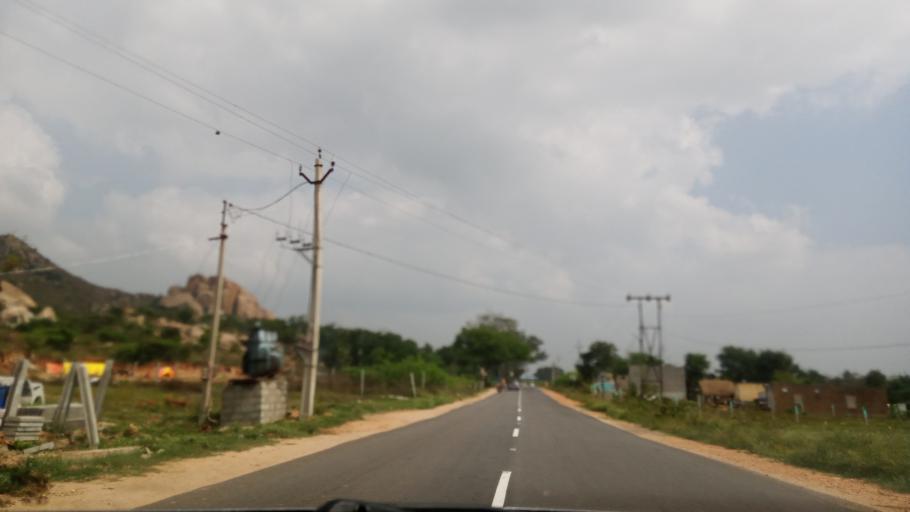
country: IN
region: Andhra Pradesh
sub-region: Chittoor
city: Madanapalle
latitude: 13.6341
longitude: 78.6170
